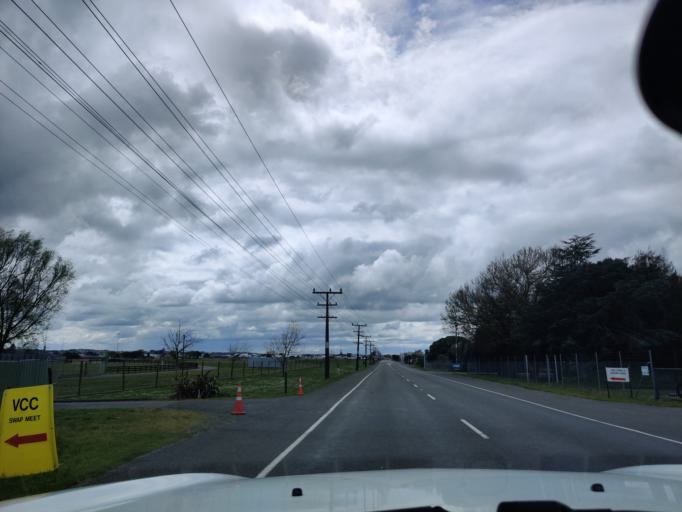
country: NZ
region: Manawatu-Wanganui
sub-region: Palmerston North City
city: Palmerston North
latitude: -40.2378
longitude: 175.5624
